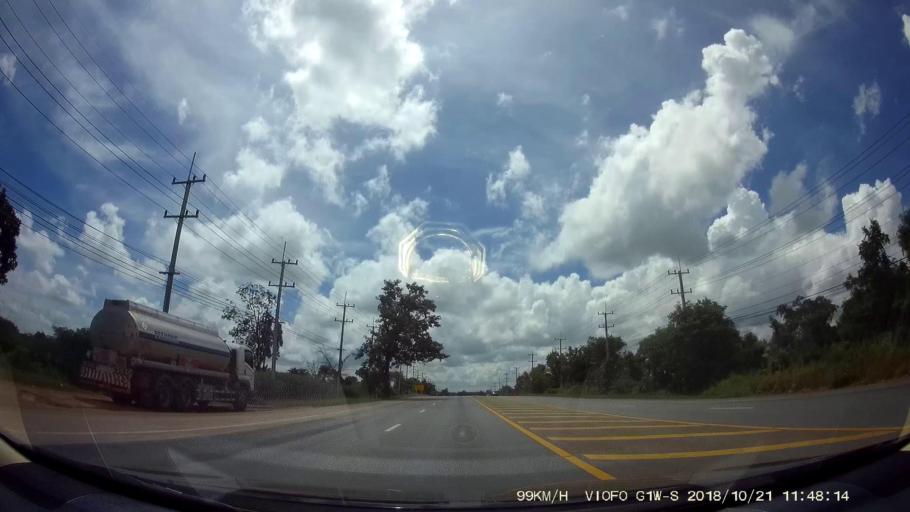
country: TH
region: Chaiyaphum
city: Noen Sa-nga
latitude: 15.6503
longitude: 101.9507
